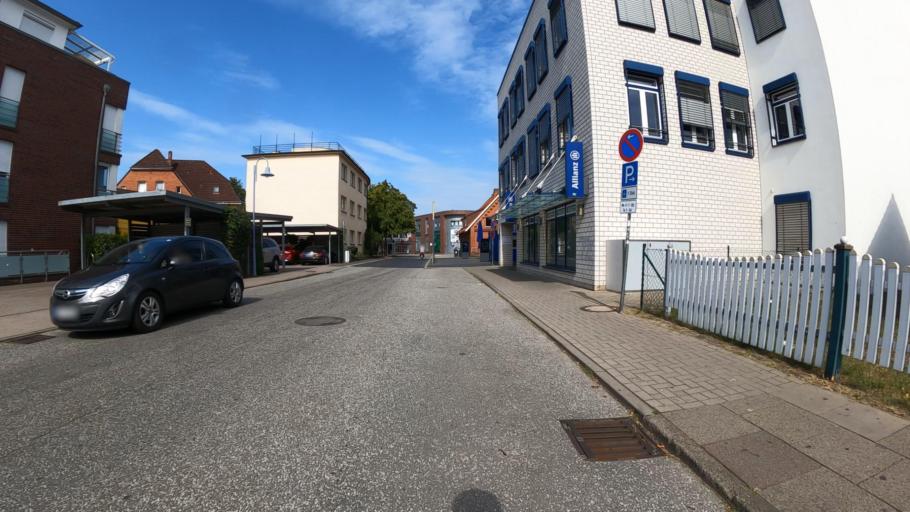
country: DE
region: Schleswig-Holstein
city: Geesthacht
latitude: 53.4326
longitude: 10.3729
